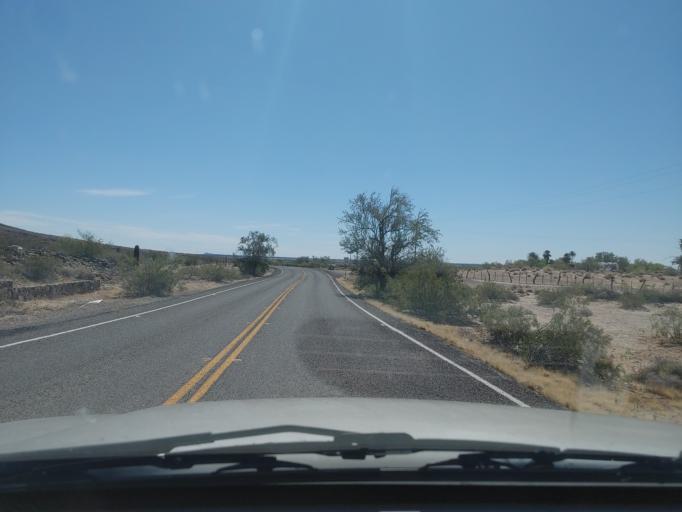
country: US
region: Arizona
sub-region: Maricopa County
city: Gila Bend
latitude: 32.9889
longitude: -113.3338
